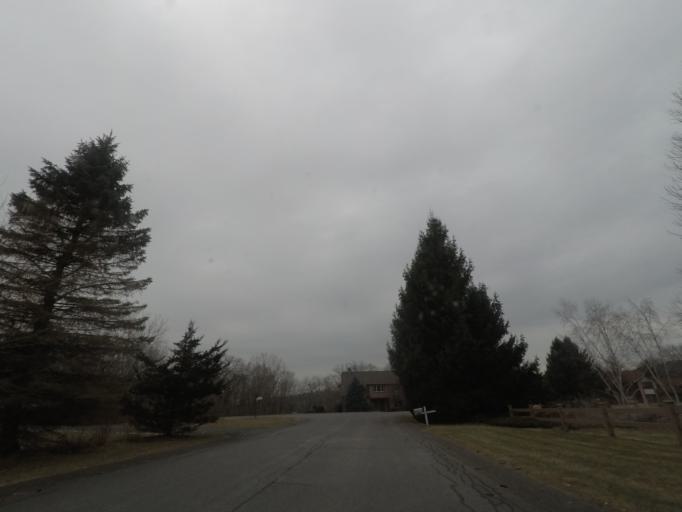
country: US
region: New York
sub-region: Rensselaer County
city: East Greenbush
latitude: 42.5634
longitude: -73.6502
